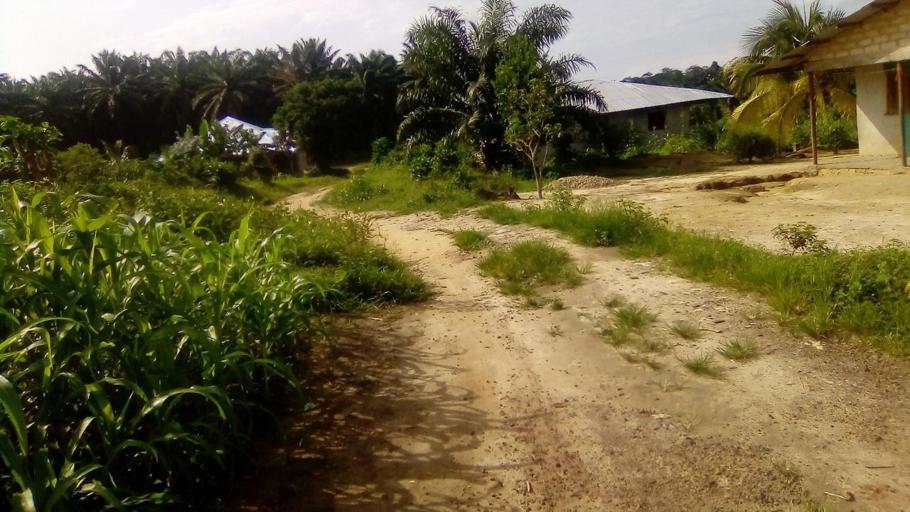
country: SL
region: Southern Province
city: Pujehun
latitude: 7.3638
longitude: -11.7221
